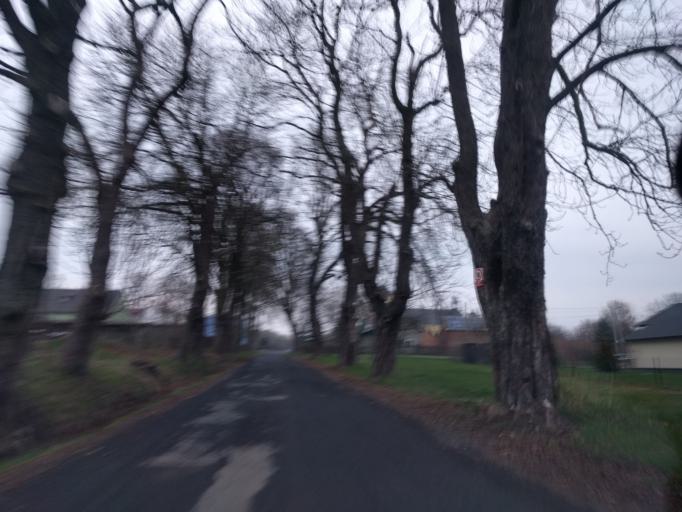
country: CZ
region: Karlovarsky
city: Bochov
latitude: 50.1313
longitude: 13.0866
